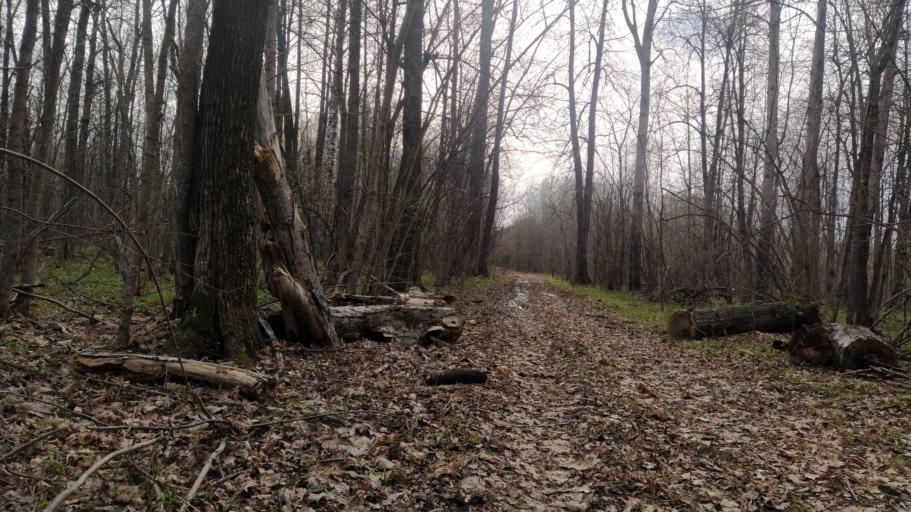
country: RU
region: Chuvashia
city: Novyye Lapsary
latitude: 56.1387
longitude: 47.1199
